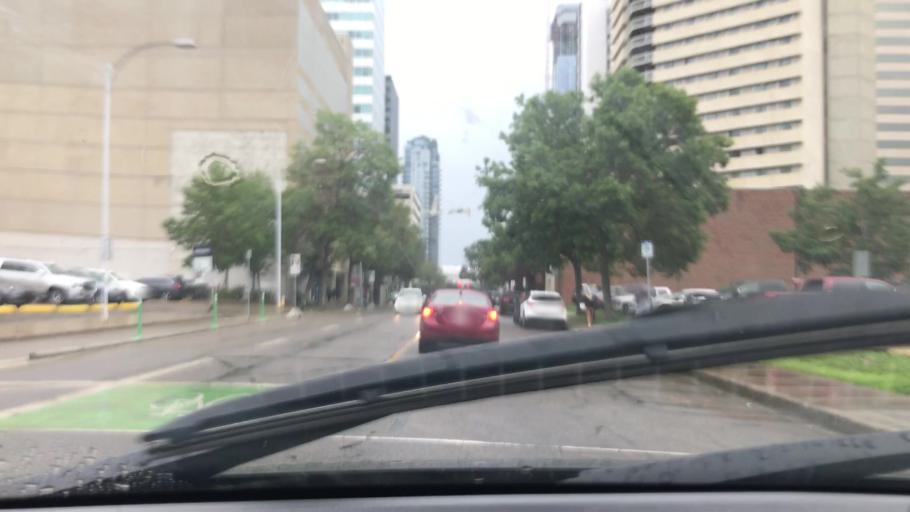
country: CA
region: Alberta
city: Edmonton
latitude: 53.5388
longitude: -113.4974
